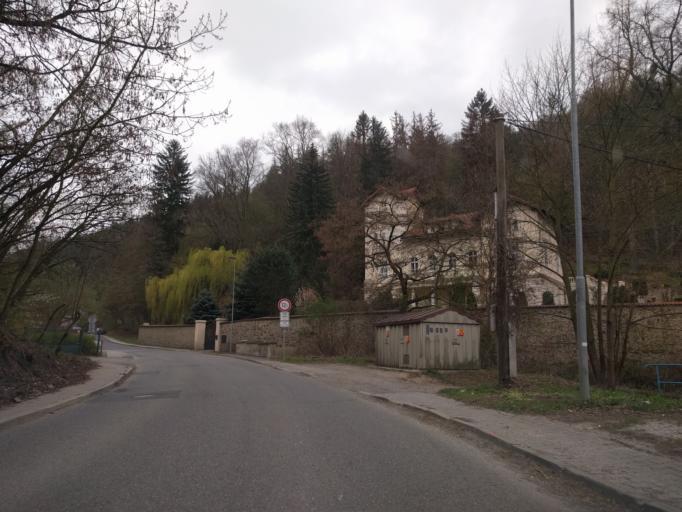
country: CZ
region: Central Bohemia
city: Vsenory
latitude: 49.9243
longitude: 14.3029
